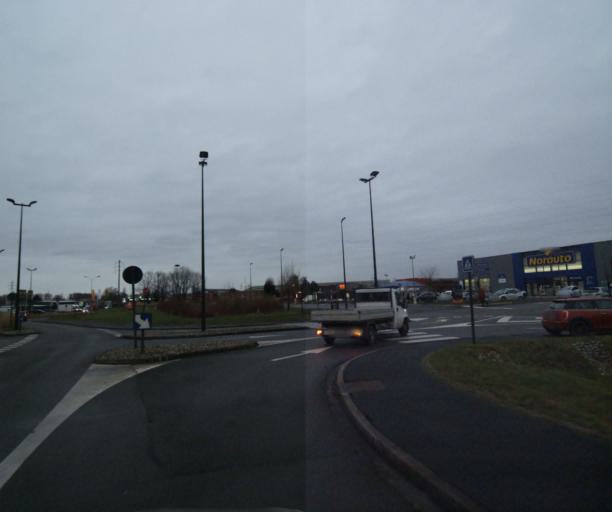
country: FR
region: Nord-Pas-de-Calais
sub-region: Departement du Nord
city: Raismes
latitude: 50.3804
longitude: 3.4784
